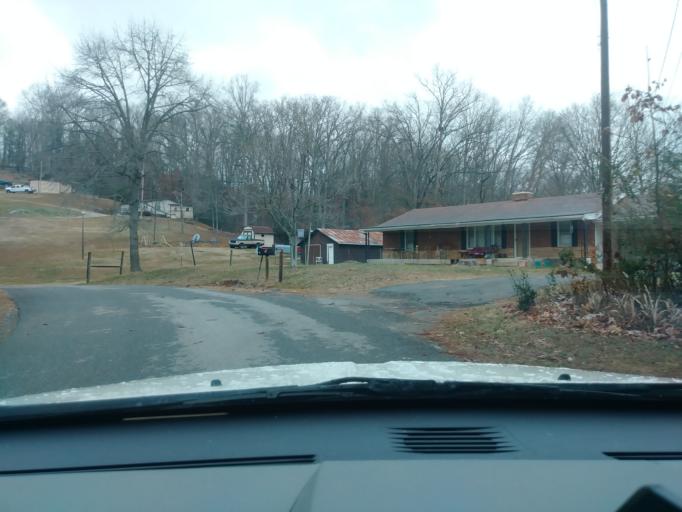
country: US
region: Tennessee
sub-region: Greene County
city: Greeneville
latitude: 36.1288
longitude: -82.8584
